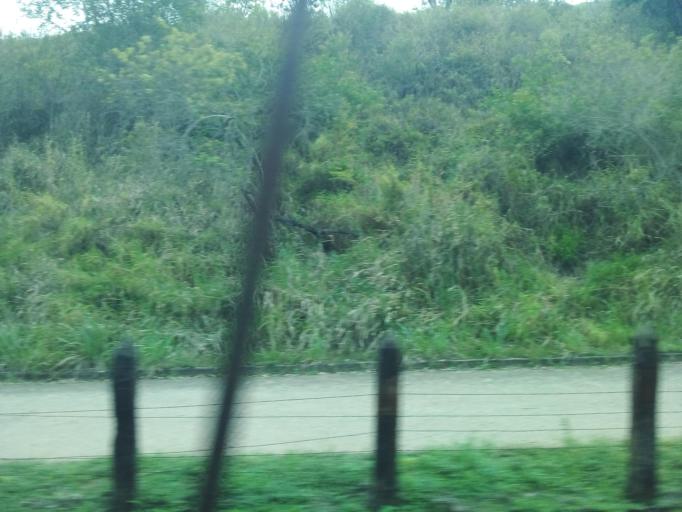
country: BR
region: Minas Gerais
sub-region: Nova Era
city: Nova Era
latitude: -19.7279
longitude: -42.9960
